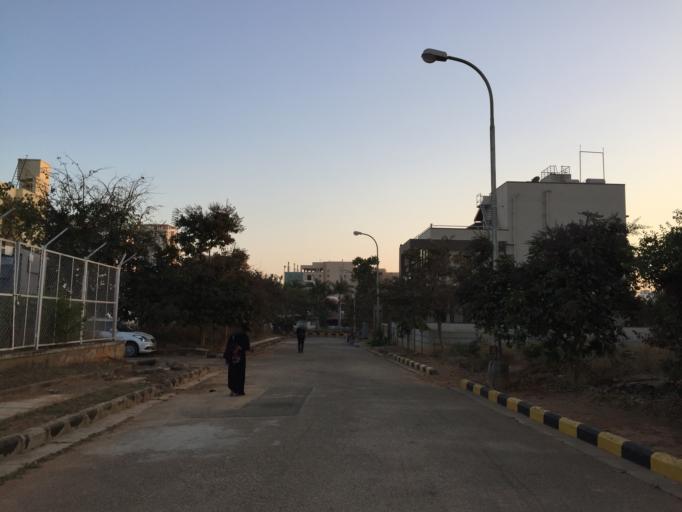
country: IN
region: Karnataka
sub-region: Bangalore Urban
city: Yelahanka
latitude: 13.0544
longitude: 77.6239
